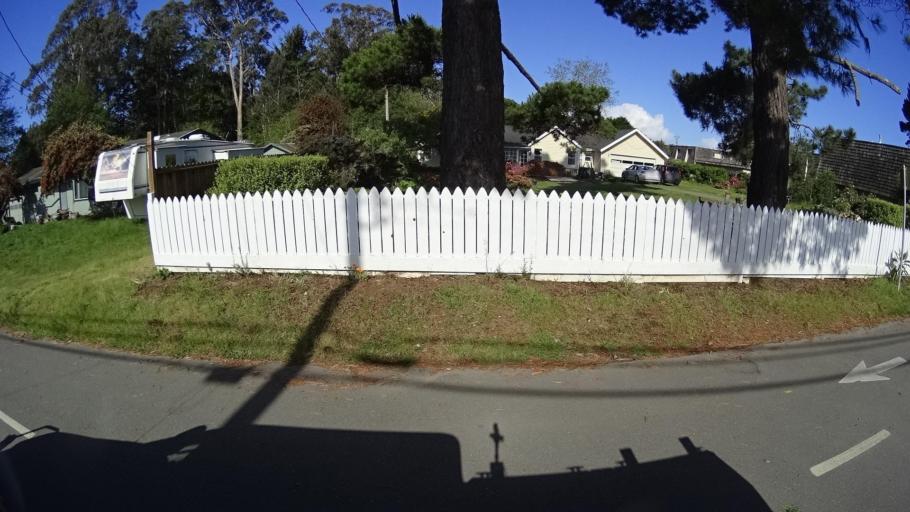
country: US
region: California
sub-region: Humboldt County
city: McKinleyville
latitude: 40.9592
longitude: -124.1105
